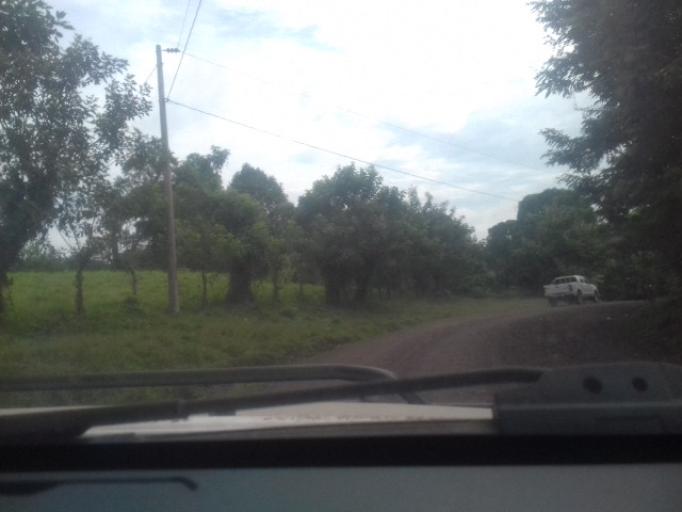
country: NI
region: Atlantico Norte (RAAN)
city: Waslala
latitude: 13.3938
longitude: -85.3261
